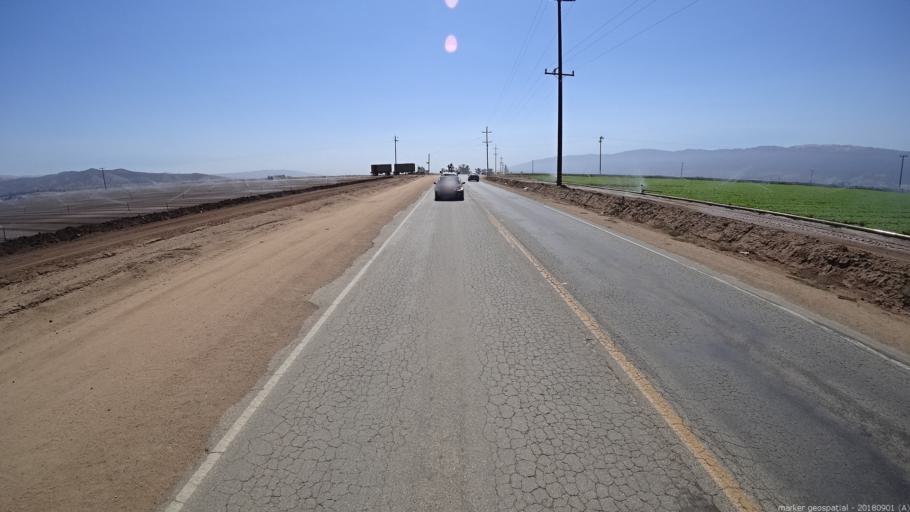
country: US
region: California
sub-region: Monterey County
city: Chualar
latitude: 36.5913
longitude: -121.5031
